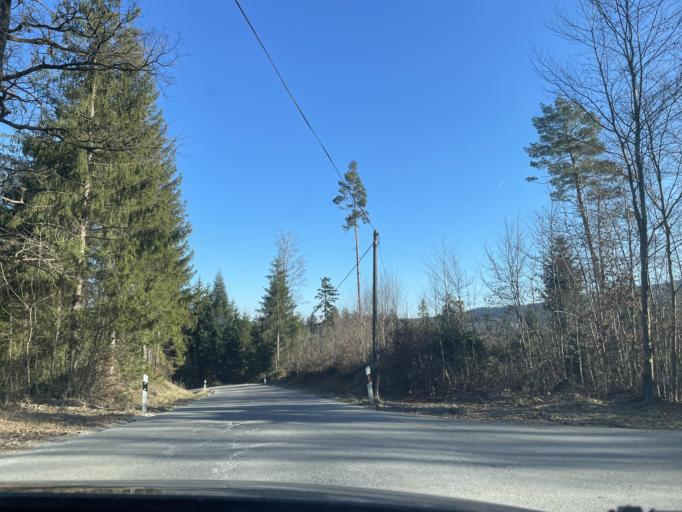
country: DE
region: Bavaria
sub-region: Lower Bavaria
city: Geiersthal
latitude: 49.0760
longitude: 12.9778
